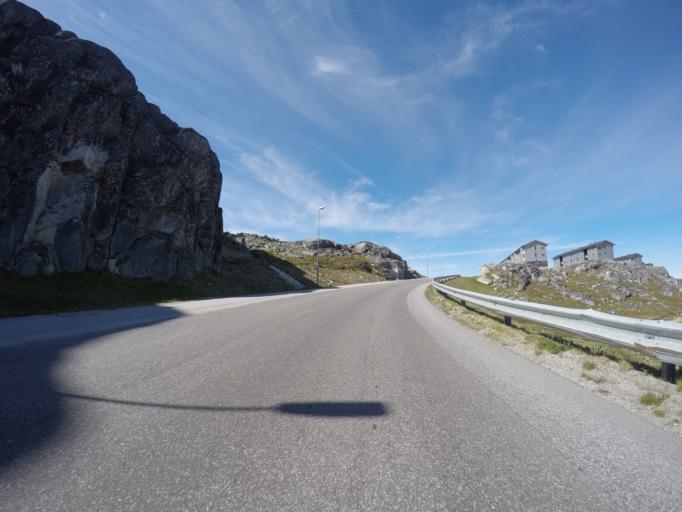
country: GL
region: Sermersooq
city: Nuuk
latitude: 64.1861
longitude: -51.7226
